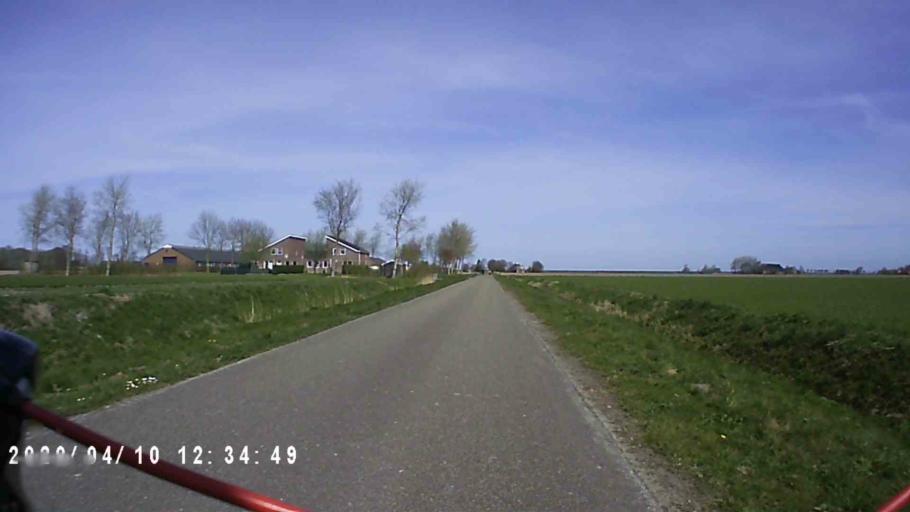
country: NL
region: Groningen
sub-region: Gemeente De Marne
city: Ulrum
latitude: 53.3980
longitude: 6.4169
